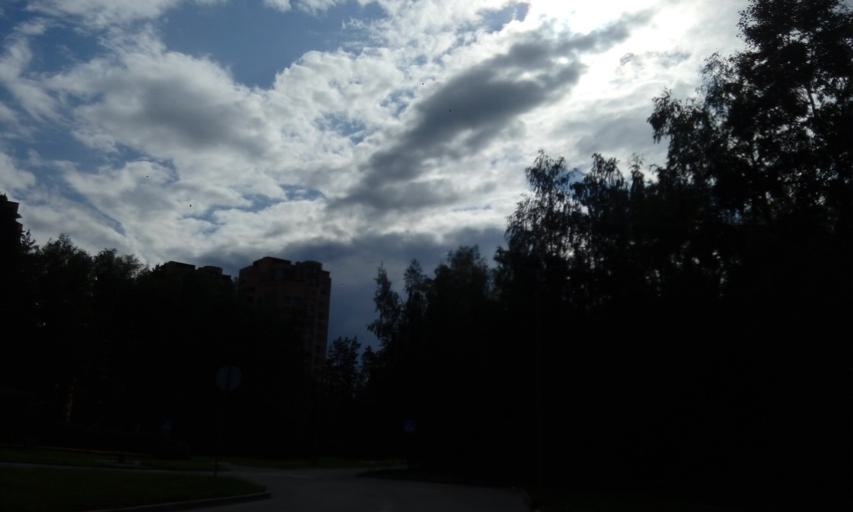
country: RU
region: Novosibirsk
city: Akademgorodok
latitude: 54.8456
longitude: 83.1031
